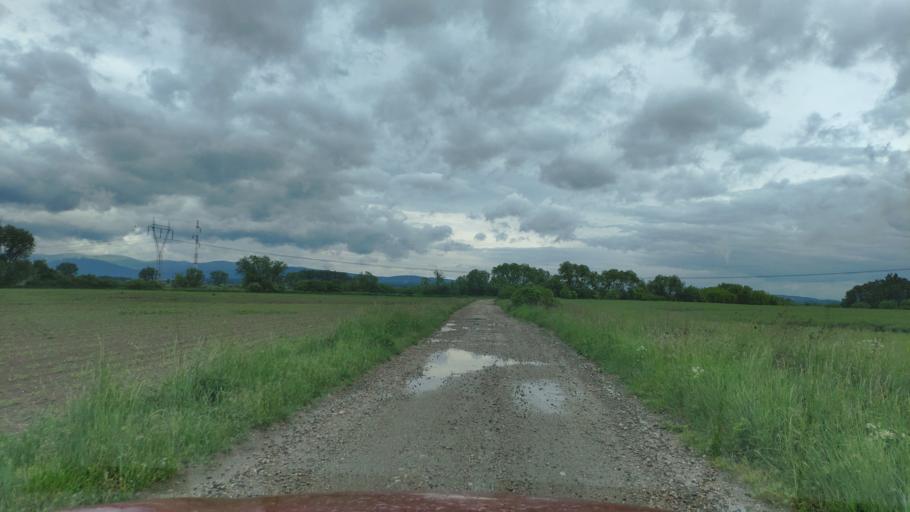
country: SK
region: Kosicky
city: Moldava nad Bodvou
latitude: 48.5596
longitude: 21.1161
